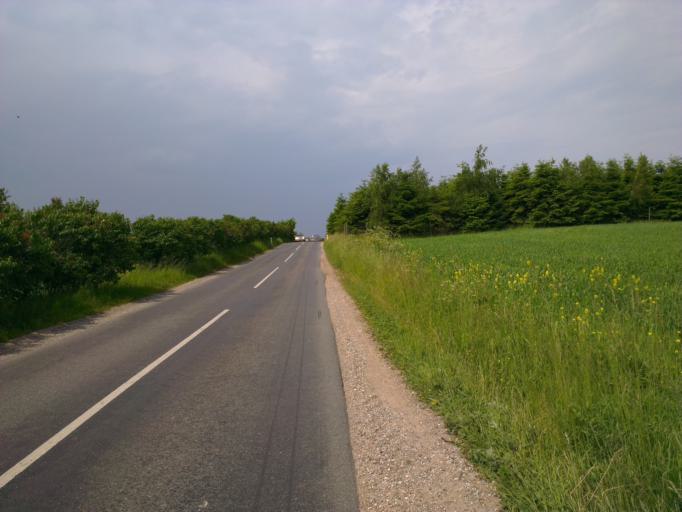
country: DK
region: Capital Region
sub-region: Frederikssund Kommune
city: Jaegerspris
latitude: 55.8270
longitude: 11.9677
